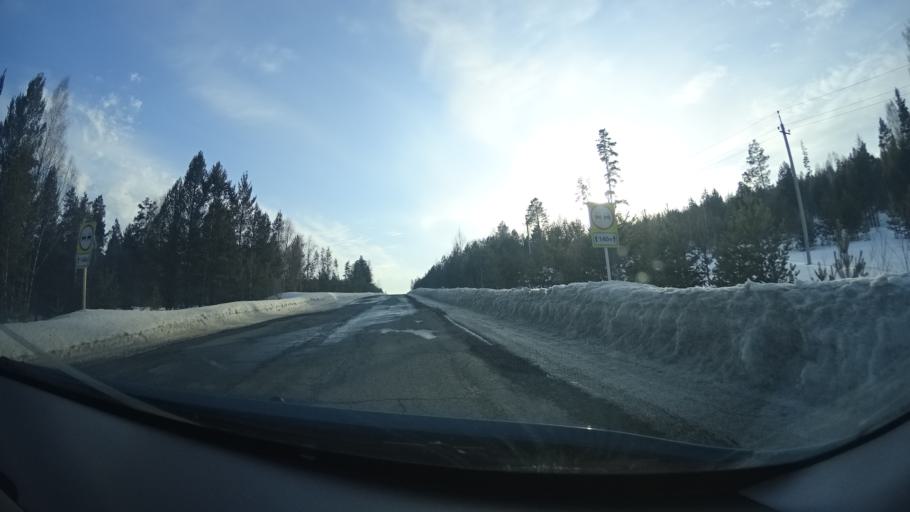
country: RU
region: Bashkortostan
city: Lomovka
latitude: 53.6555
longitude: 58.2133
